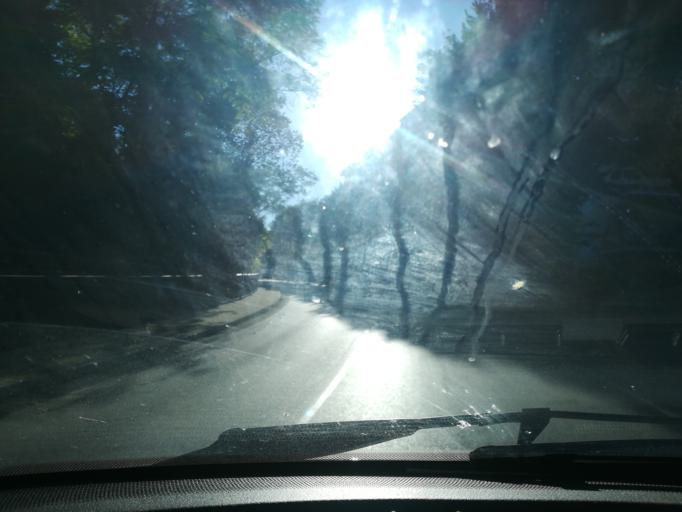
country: IT
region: The Marches
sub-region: Provincia di Macerata
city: Tolentino
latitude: 43.2107
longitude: 13.2903
